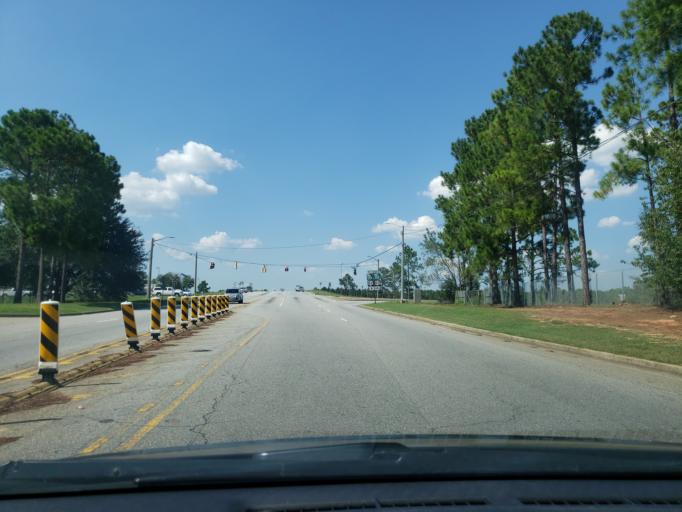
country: US
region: Georgia
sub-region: Dougherty County
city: Albany
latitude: 31.6144
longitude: -84.2042
